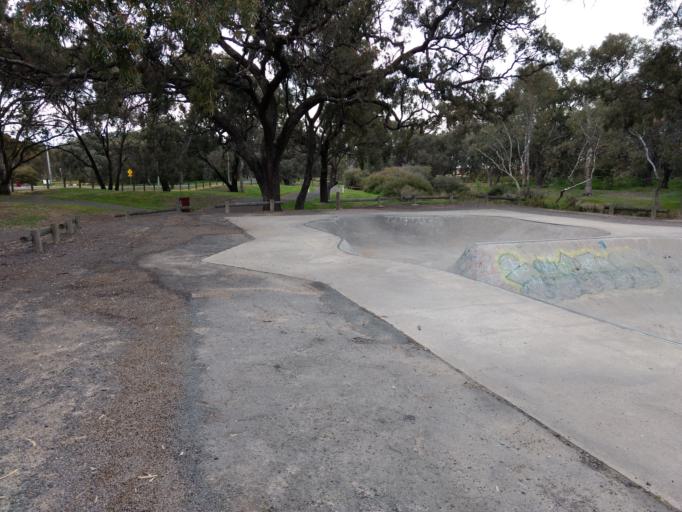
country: AU
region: Victoria
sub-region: Horsham
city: Horsham
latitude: -36.7204
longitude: 142.1963
